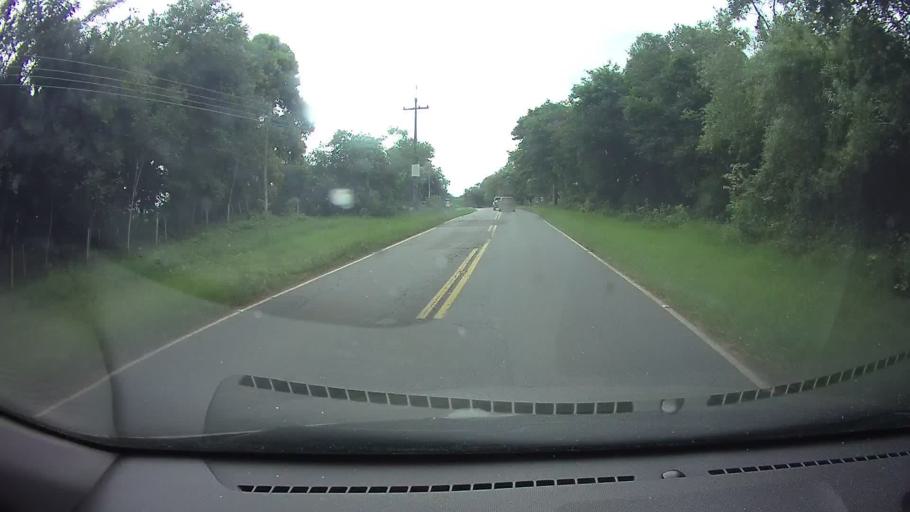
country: PY
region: Central
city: Nueva Italia
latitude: -25.5697
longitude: -57.5035
